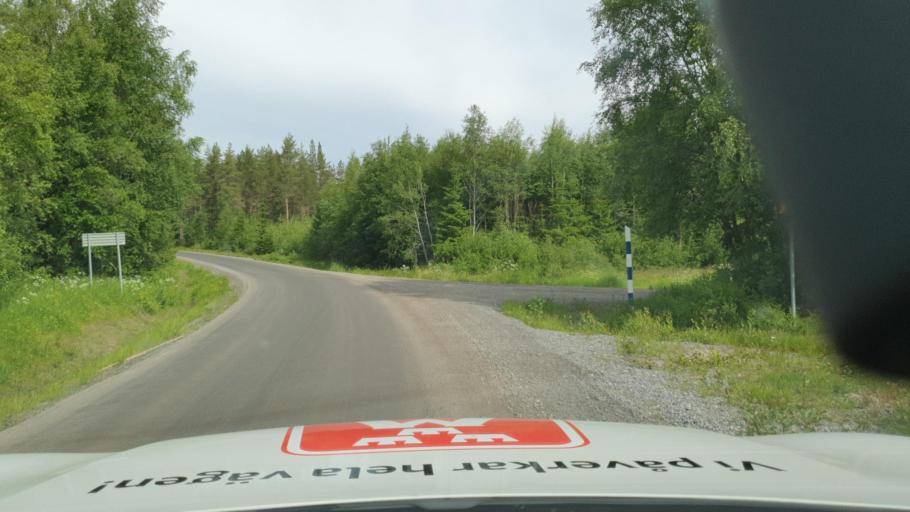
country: SE
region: Vaesterbotten
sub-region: Robertsfors Kommun
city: Robertsfors
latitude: 64.0366
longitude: 20.8832
